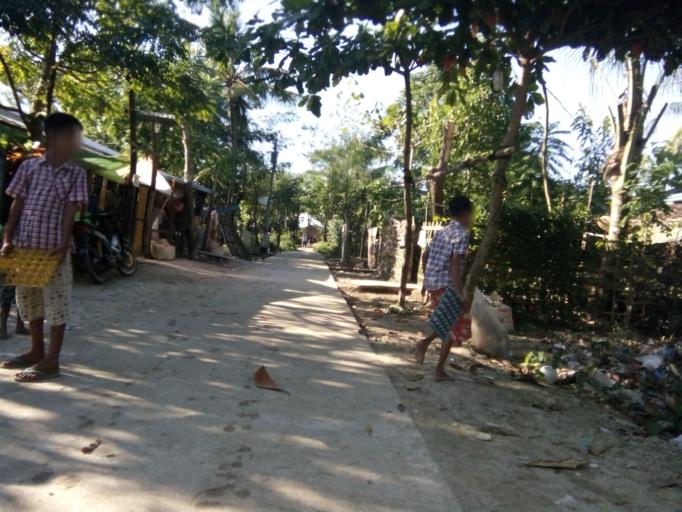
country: MM
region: Yangon
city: Kanbe
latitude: 16.8745
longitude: 95.9785
